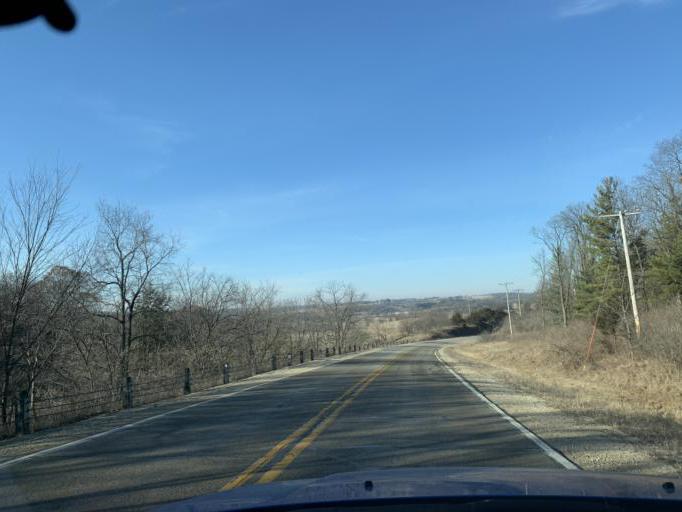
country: US
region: Wisconsin
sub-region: Green County
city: New Glarus
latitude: 42.7813
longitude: -89.8599
